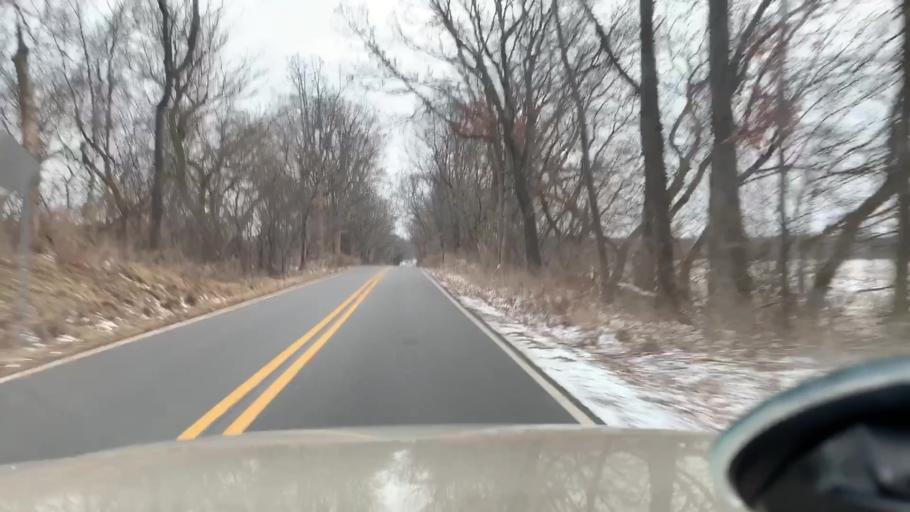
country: US
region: Michigan
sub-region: Jackson County
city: Spring Arbor
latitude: 42.2090
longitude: -84.5309
